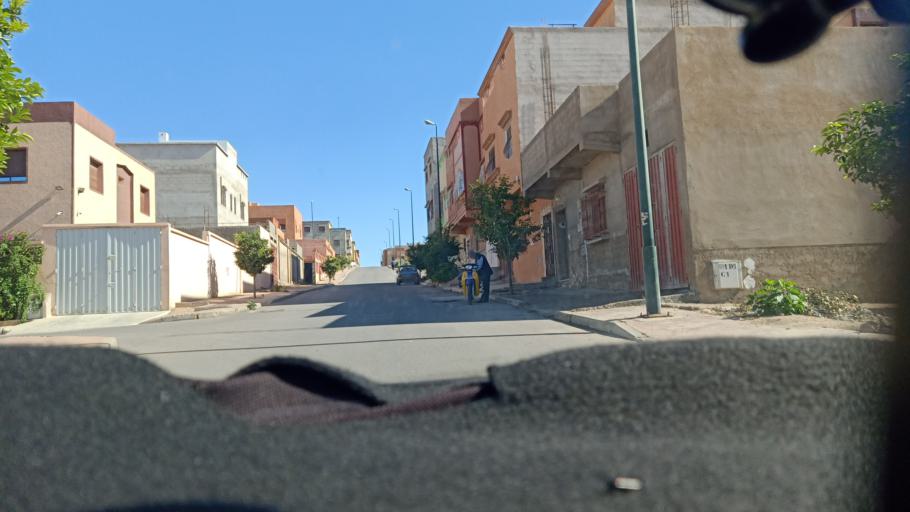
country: MA
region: Doukkala-Abda
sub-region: Safi
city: Youssoufia
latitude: 32.2397
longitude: -8.5334
